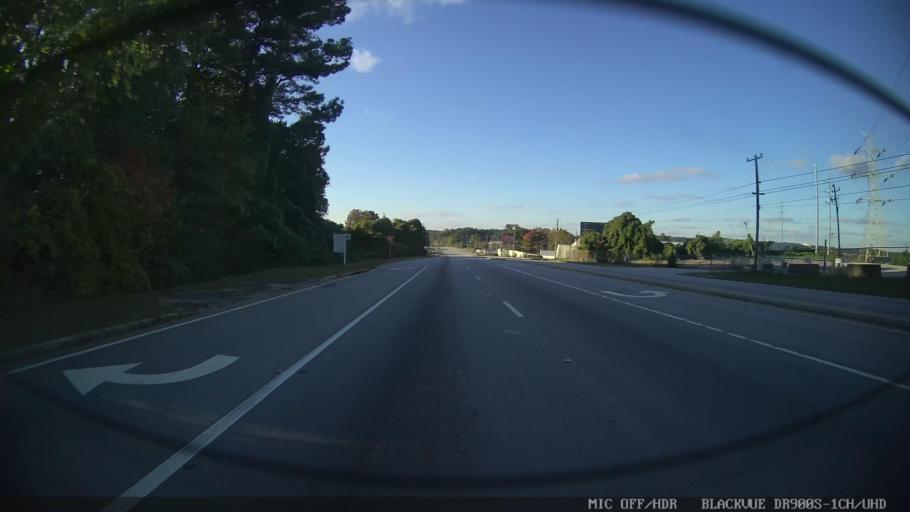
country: US
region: Georgia
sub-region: Clayton County
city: Conley
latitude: 33.6402
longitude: -84.3220
